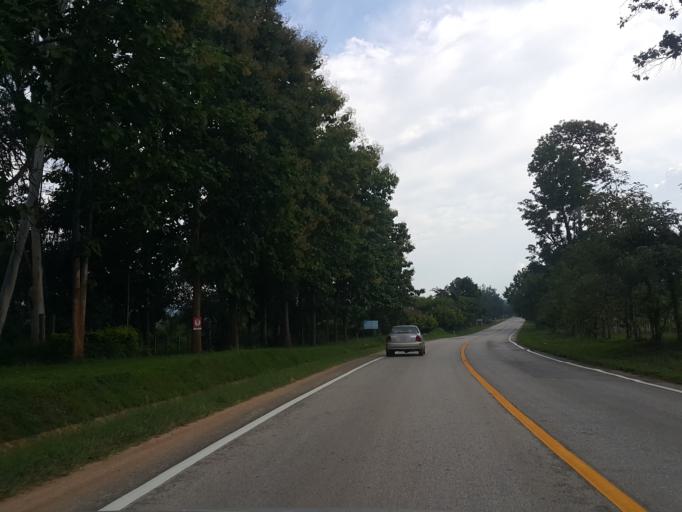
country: TH
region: Chiang Mai
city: Phrao
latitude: 19.2794
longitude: 99.1892
